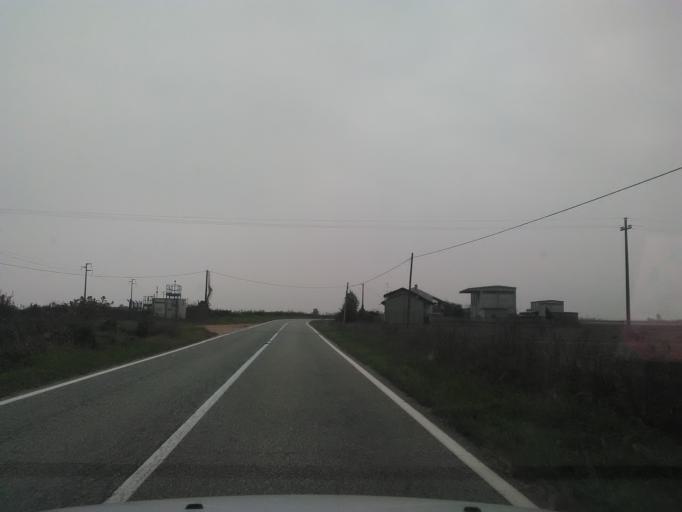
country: IT
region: Piedmont
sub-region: Provincia di Vercelli
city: Livorno Ferraris
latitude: 45.2802
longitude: 8.1060
